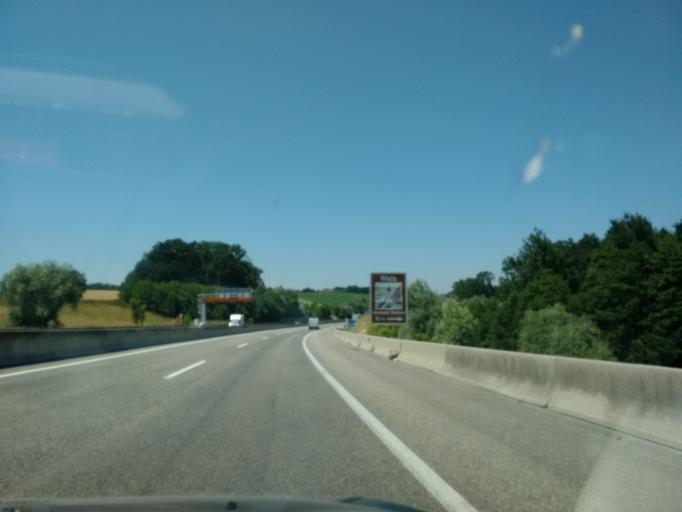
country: AT
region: Upper Austria
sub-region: Wels-Land
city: Sattledt
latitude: 48.0733
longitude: 14.0225
